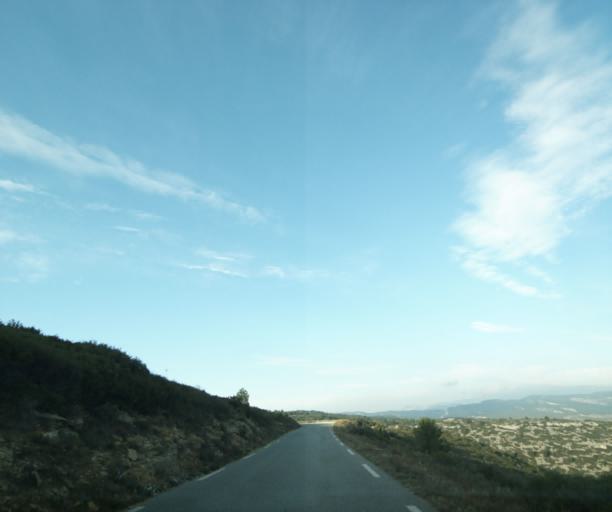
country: FR
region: Provence-Alpes-Cote d'Azur
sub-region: Departement des Bouches-du-Rhone
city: Cassis
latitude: 43.1911
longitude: 5.5590
